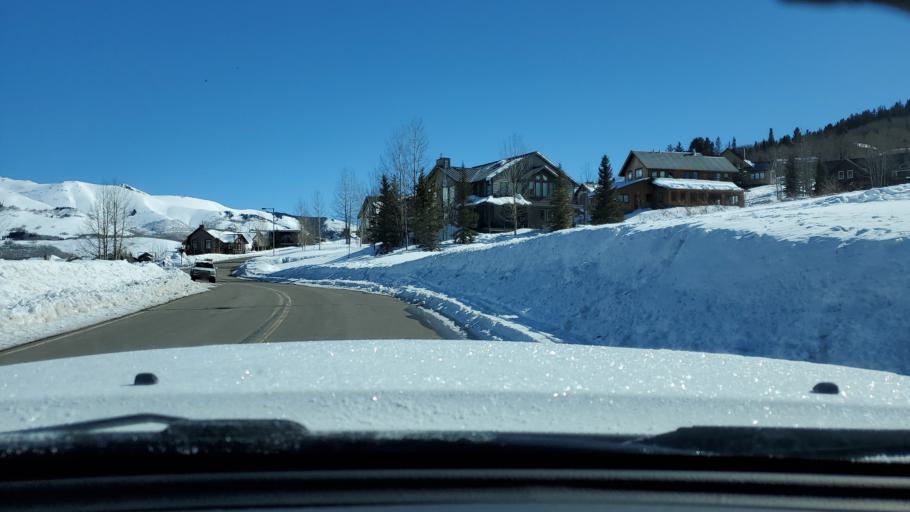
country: US
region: Colorado
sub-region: Gunnison County
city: Crested Butte
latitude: 38.9110
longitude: -106.9635
